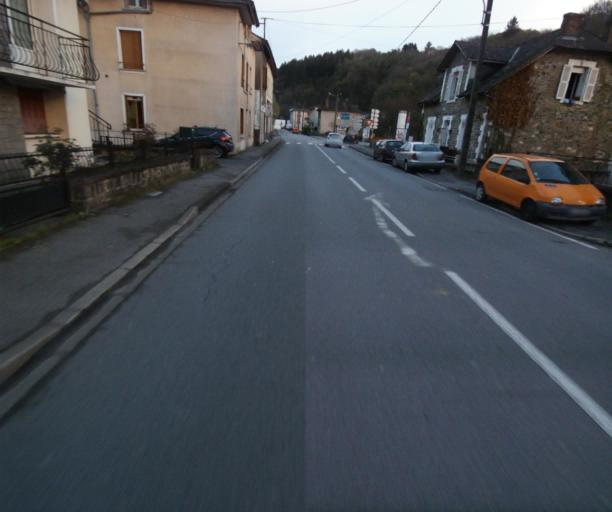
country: FR
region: Limousin
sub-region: Departement de la Correze
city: Tulle
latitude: 45.2513
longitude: 1.7655
